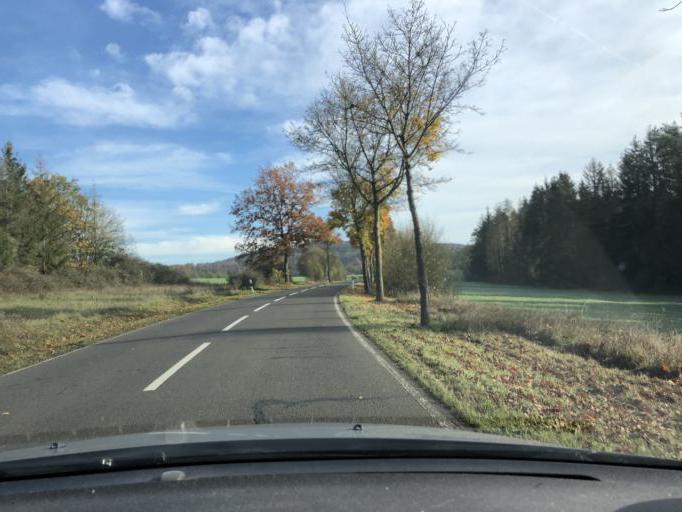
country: DE
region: Thuringia
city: Reurieth
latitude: 50.4355
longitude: 10.6367
